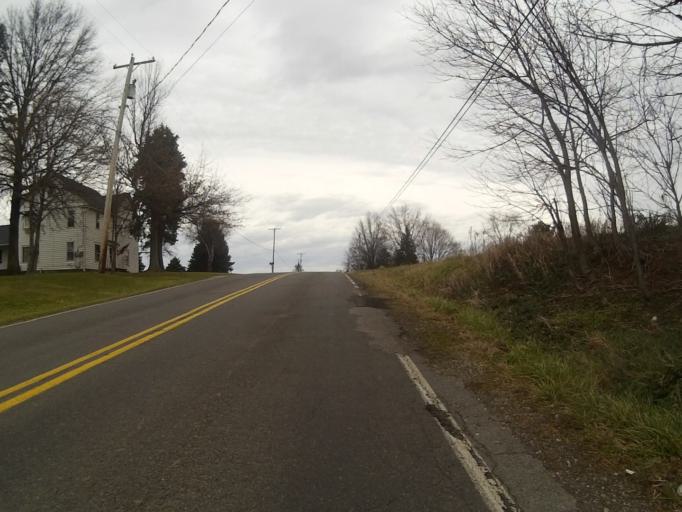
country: US
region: Ohio
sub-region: Stark County
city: Hartville
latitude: 41.0100
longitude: -81.3294
